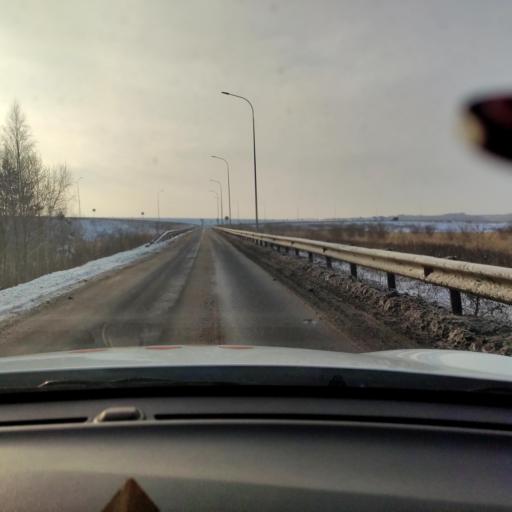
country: RU
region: Tatarstan
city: Sviyazhsk
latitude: 55.7415
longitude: 48.7850
